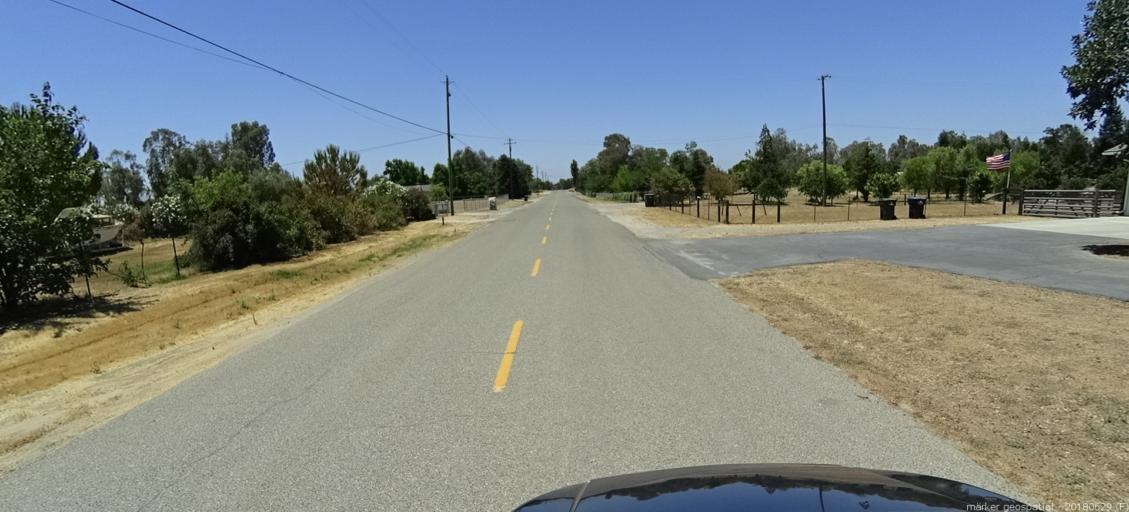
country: US
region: California
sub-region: Madera County
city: Parksdale
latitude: 36.9930
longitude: -119.9798
